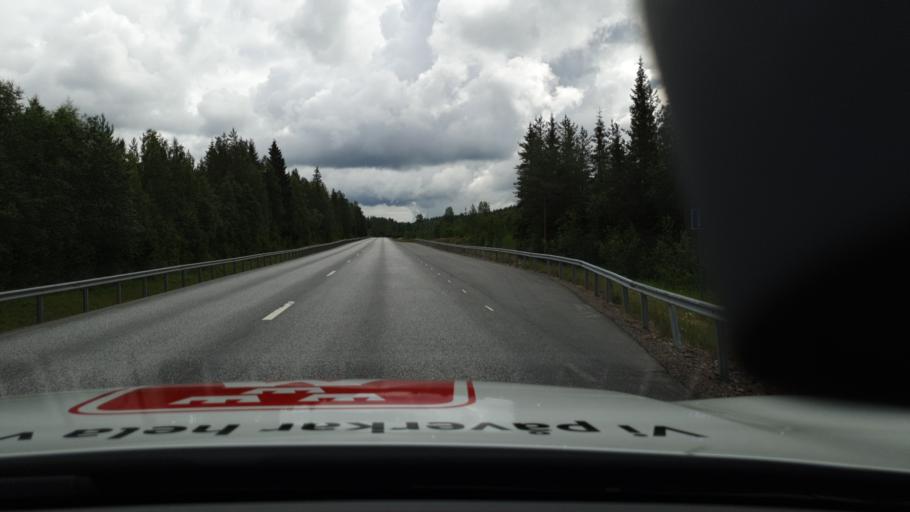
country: SE
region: Norrbotten
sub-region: Pitea Kommun
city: Norrfjarden
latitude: 65.6081
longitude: 21.4645
